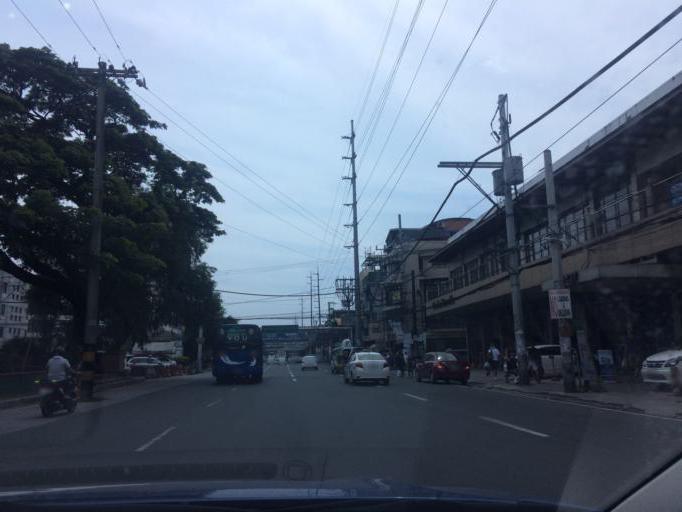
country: PH
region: Metro Manila
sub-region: Makati City
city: Makati City
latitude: 14.5549
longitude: 120.9997
